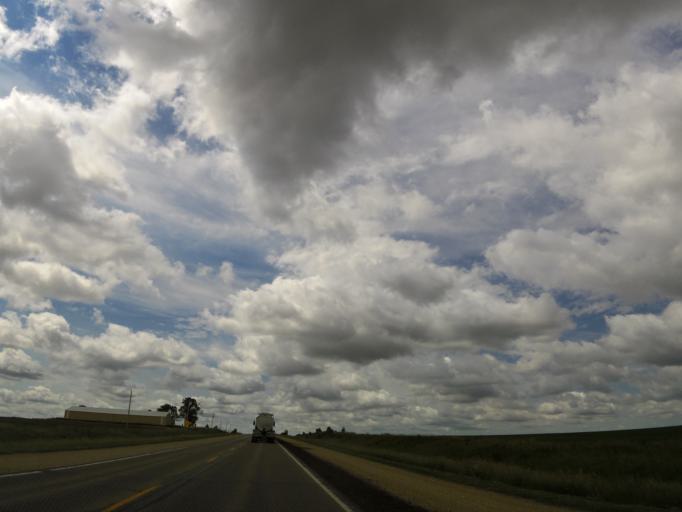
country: US
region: Iowa
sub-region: Howard County
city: Cresco
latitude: 43.3254
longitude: -92.2990
